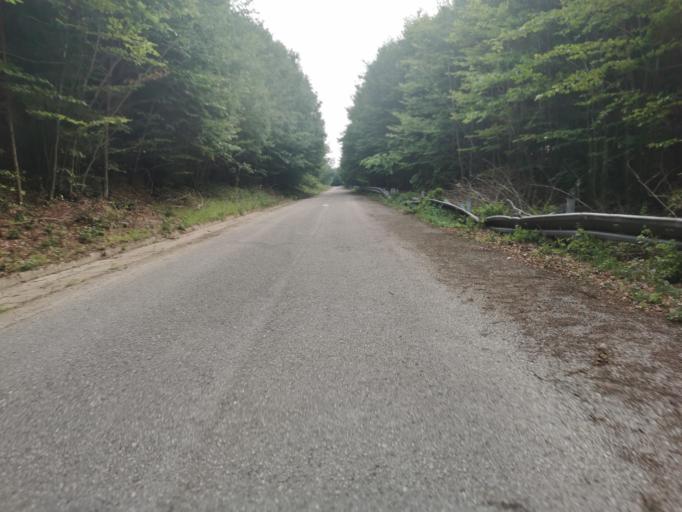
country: SK
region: Trenciansky
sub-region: Okres Myjava
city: Myjava
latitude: 48.8354
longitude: 17.6125
